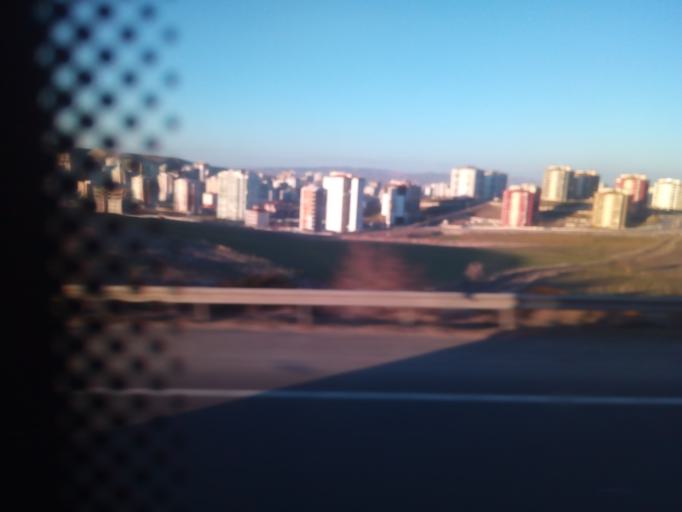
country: TR
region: Ankara
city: Etimesgut
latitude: 39.8814
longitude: 32.6179
